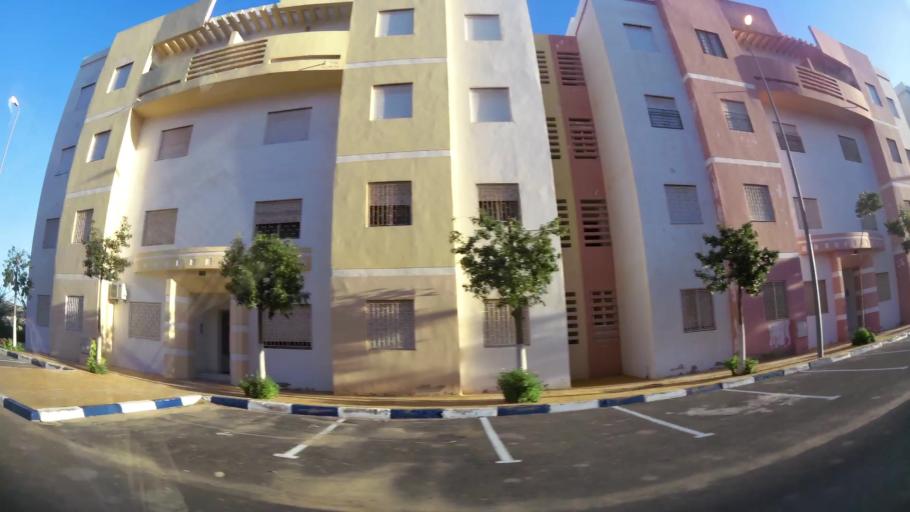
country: MA
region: Oriental
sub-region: Berkane-Taourirt
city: Madagh
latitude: 35.0748
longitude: -2.2361
